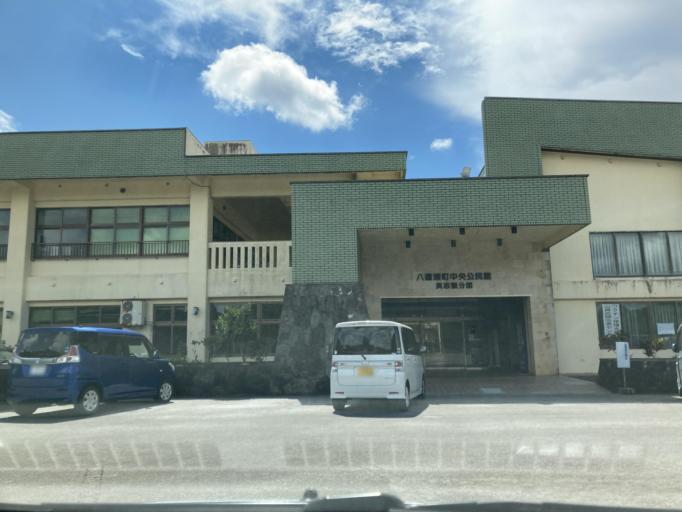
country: JP
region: Okinawa
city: Itoman
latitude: 26.1199
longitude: 127.7443
